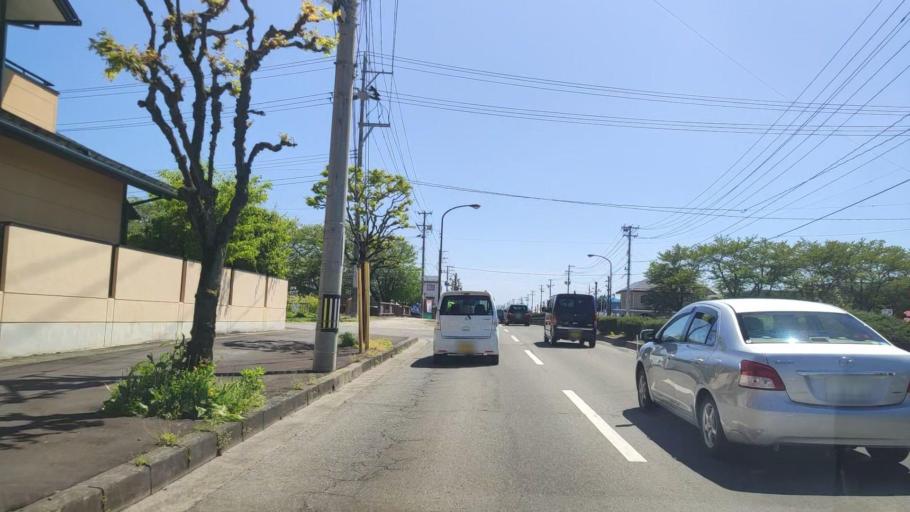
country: JP
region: Yamagata
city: Tendo
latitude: 38.3629
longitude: 140.3666
